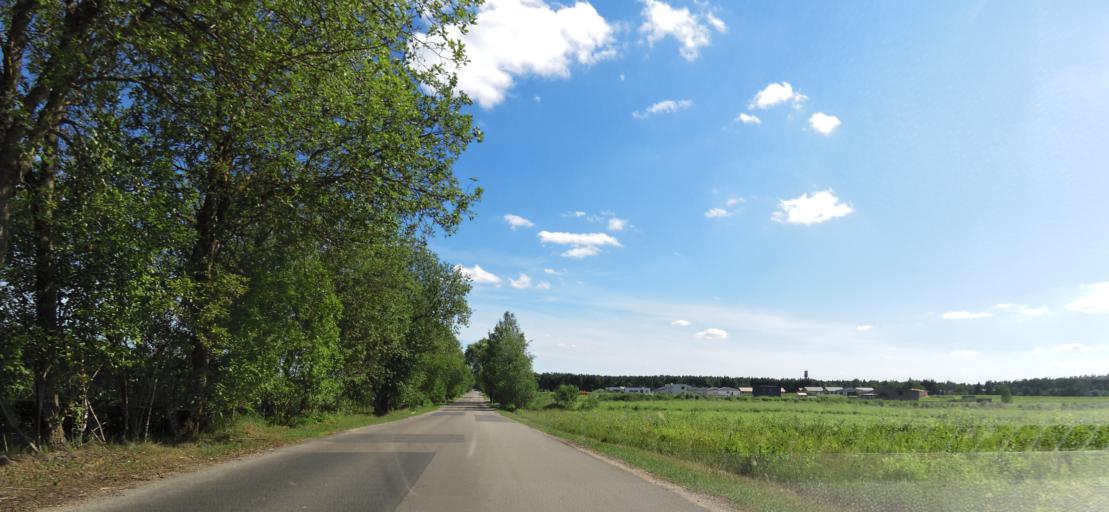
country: LT
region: Vilnius County
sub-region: Vilnius
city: Fabijoniskes
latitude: 54.8106
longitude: 25.3241
